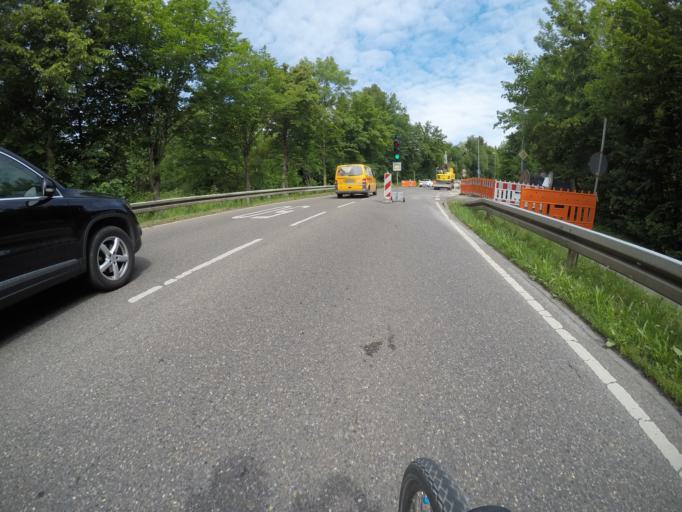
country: DE
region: Baden-Wuerttemberg
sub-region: Regierungsbezirk Stuttgart
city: Kirchheim unter Teck
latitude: 48.6569
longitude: 9.4578
